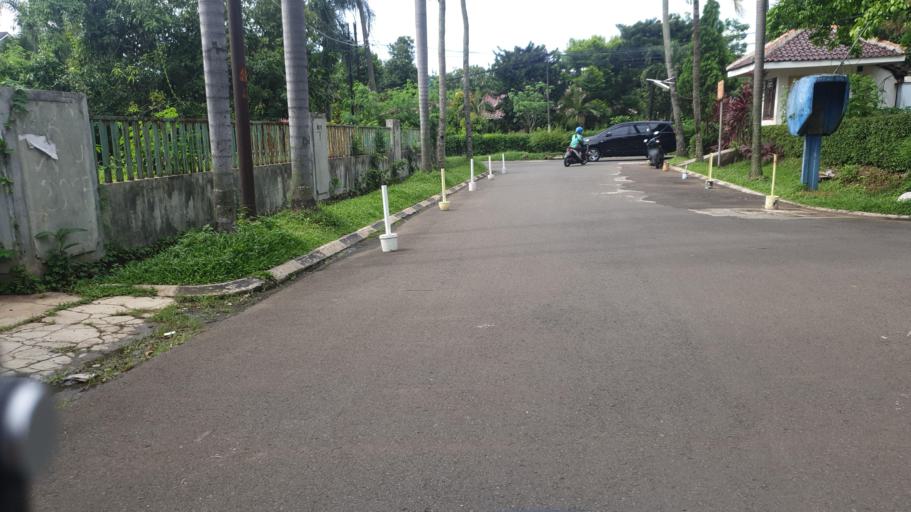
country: ID
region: West Java
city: Pamulang
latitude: -6.2955
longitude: 106.7921
